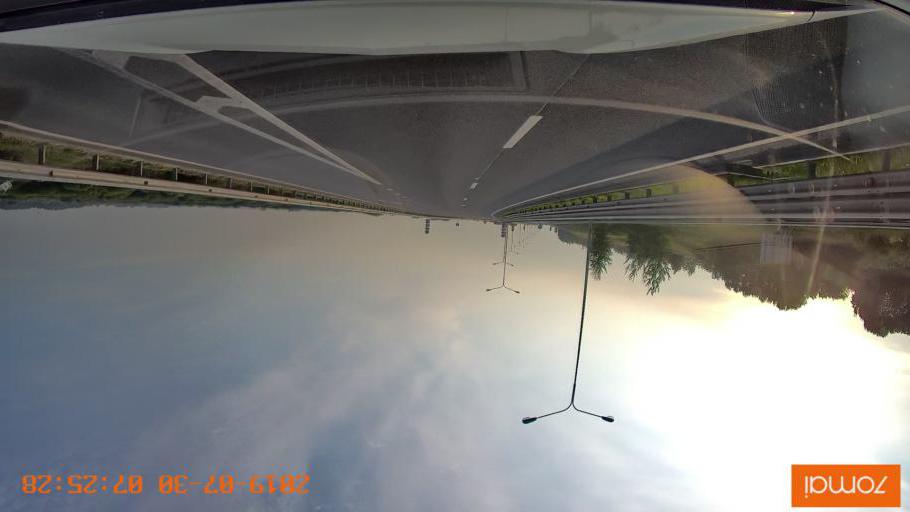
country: RU
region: Kaliningrad
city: Gvardeysk
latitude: 54.6865
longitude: 20.8360
